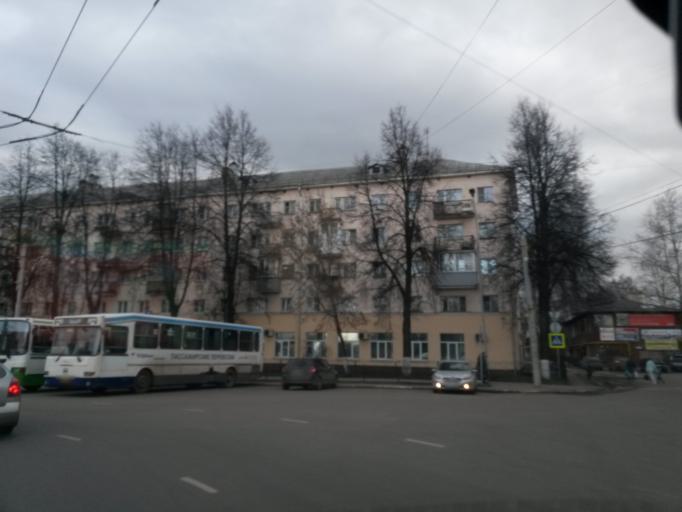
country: RU
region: Jaroslavl
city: Yaroslavl
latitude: 57.6268
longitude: 39.8361
